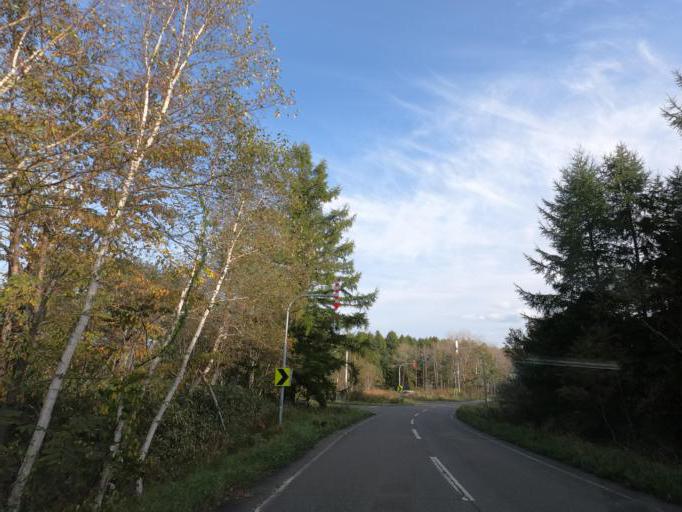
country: JP
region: Hokkaido
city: Obihiro
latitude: 42.5301
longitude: 143.3819
